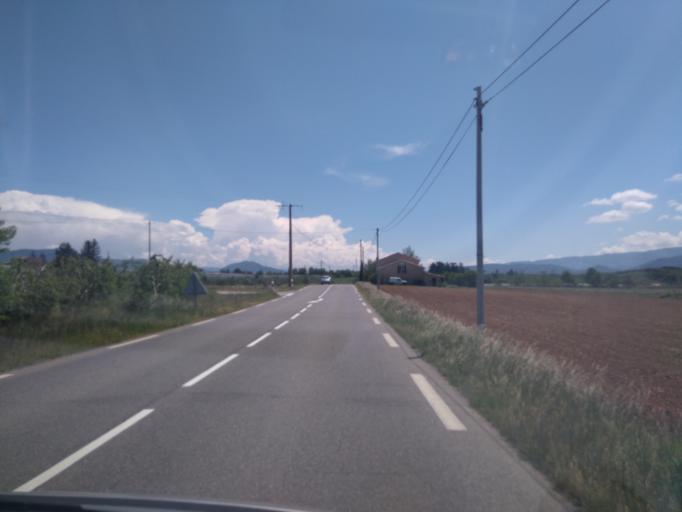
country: FR
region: Provence-Alpes-Cote d'Azur
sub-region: Departement des Hautes-Alpes
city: Laragne-Monteglin
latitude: 44.2790
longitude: 5.8496
